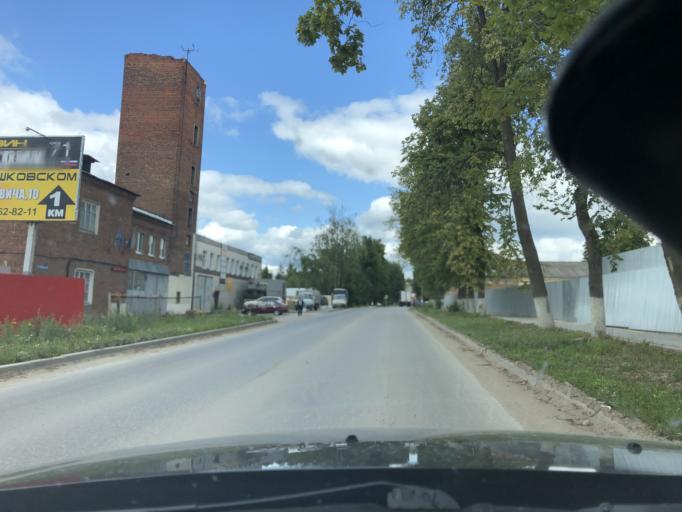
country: RU
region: Tula
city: Yasnogorsk
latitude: 54.4753
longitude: 37.6981
